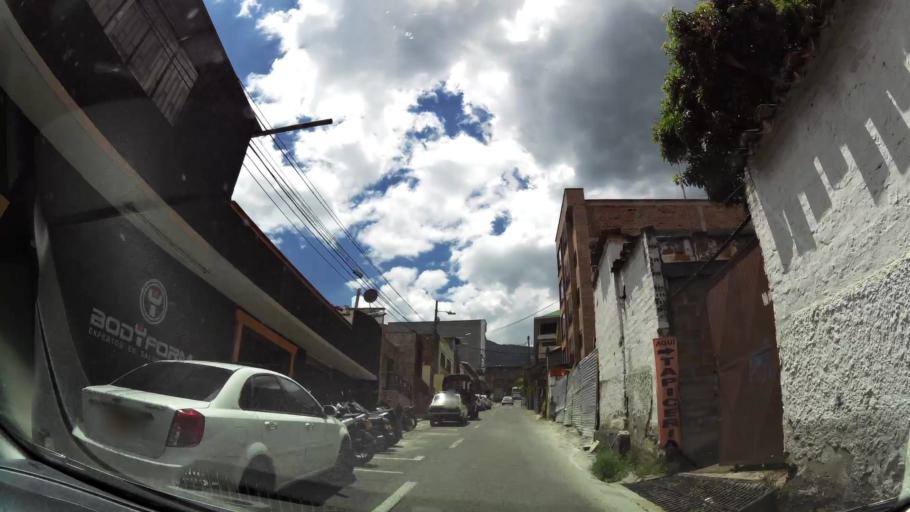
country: CO
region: Antioquia
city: La Estrella
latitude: 6.1590
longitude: -75.6437
